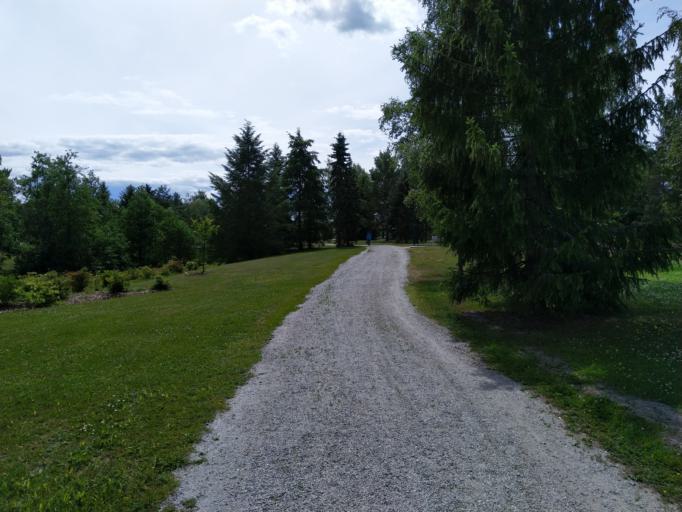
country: FI
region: Varsinais-Suomi
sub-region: Salo
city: Halikko
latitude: 60.3990
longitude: 23.0818
